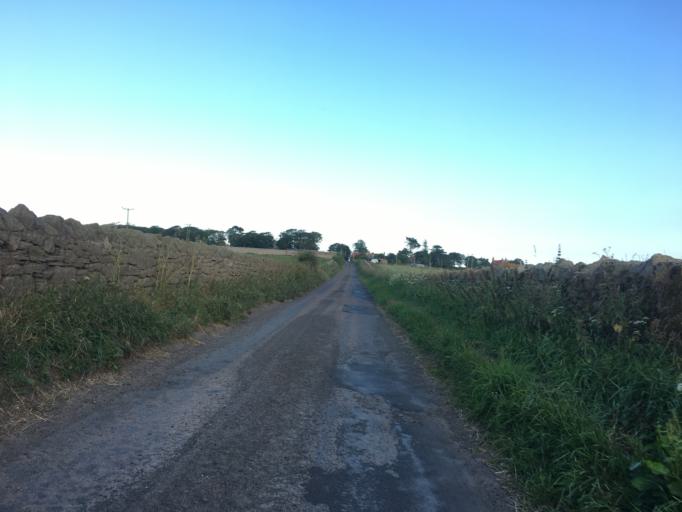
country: GB
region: England
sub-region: Northumberland
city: North Sunderland
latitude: 55.5893
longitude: -1.6827
